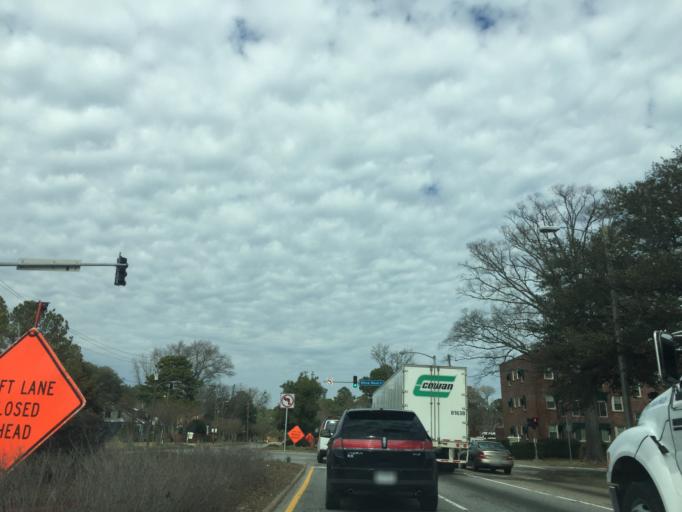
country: US
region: Virginia
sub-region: City of Norfolk
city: Norfolk
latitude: 36.8901
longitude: -76.2790
